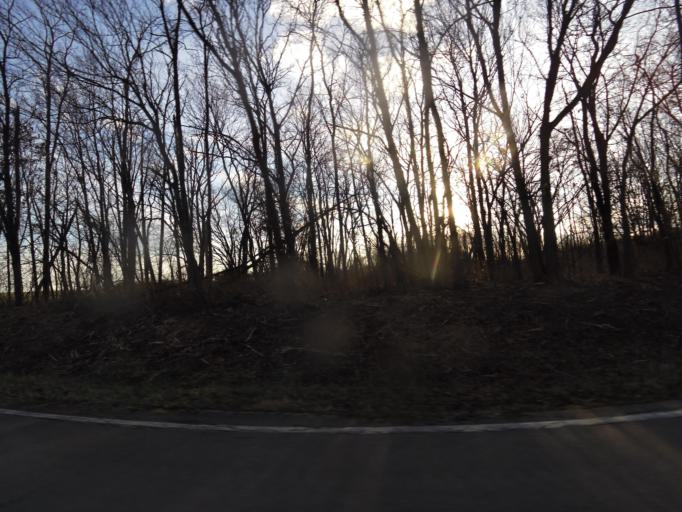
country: US
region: Illinois
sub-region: Fayette County
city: Vandalia
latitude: 38.9258
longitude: -89.1987
